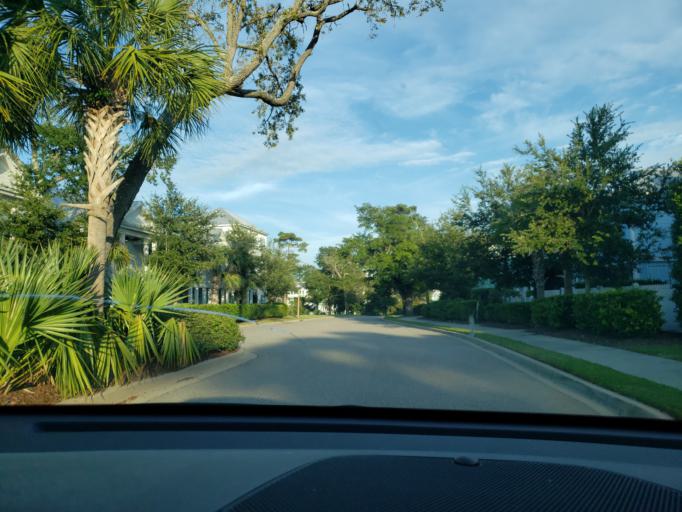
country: US
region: South Carolina
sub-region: Horry County
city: North Myrtle Beach
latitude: 33.7932
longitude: -78.7380
